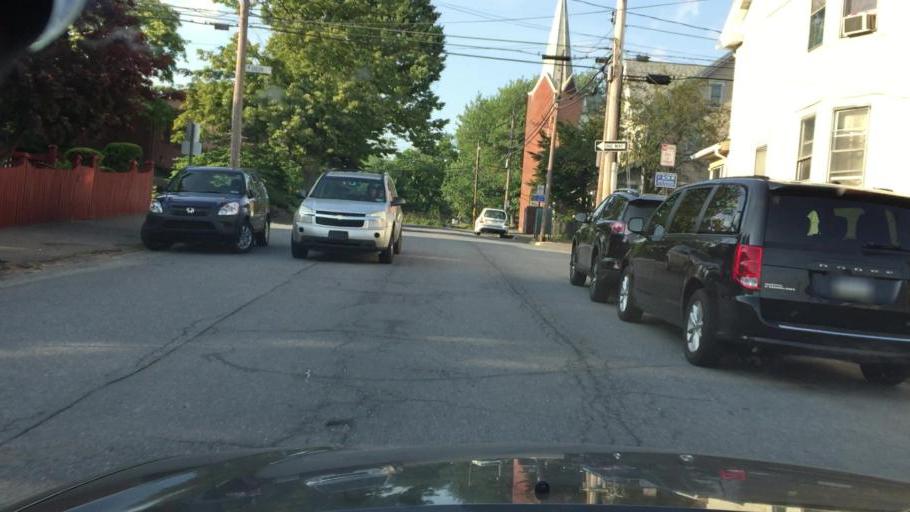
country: US
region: Pennsylvania
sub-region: Luzerne County
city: Hazleton
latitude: 40.9566
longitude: -75.9800
